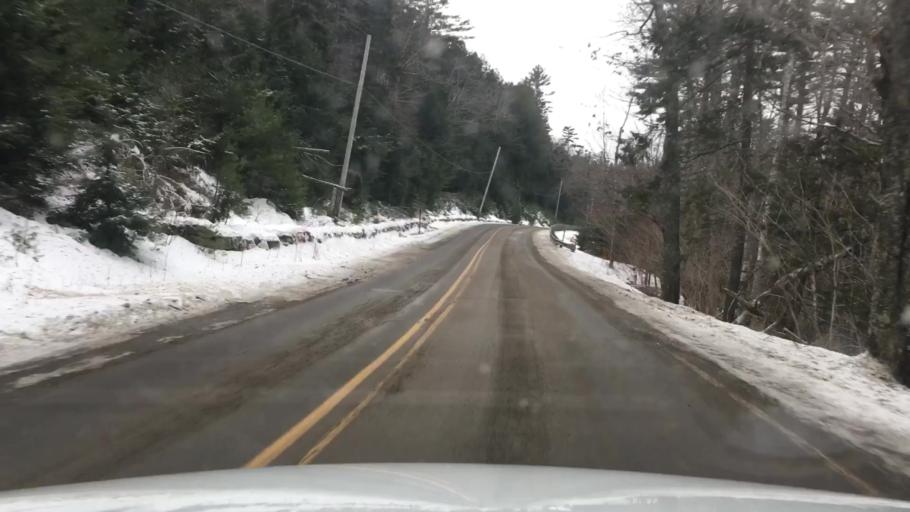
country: US
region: Maine
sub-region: Waldo County
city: Lincolnville
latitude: 44.2872
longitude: -69.0177
